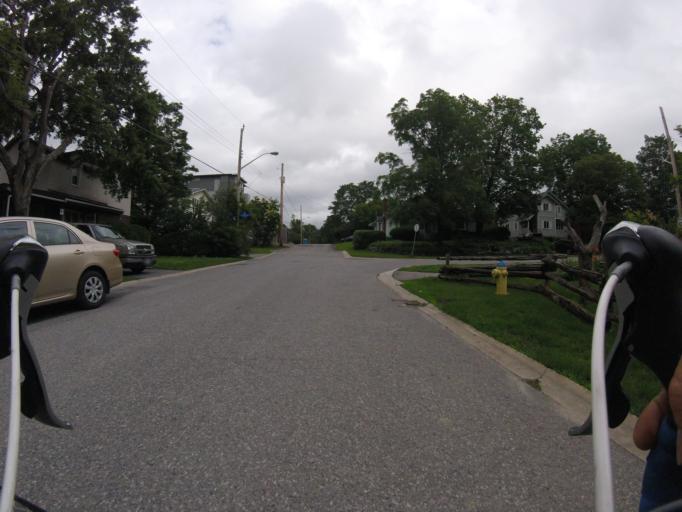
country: CA
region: Ontario
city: Ottawa
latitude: 45.3890
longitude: -75.7573
